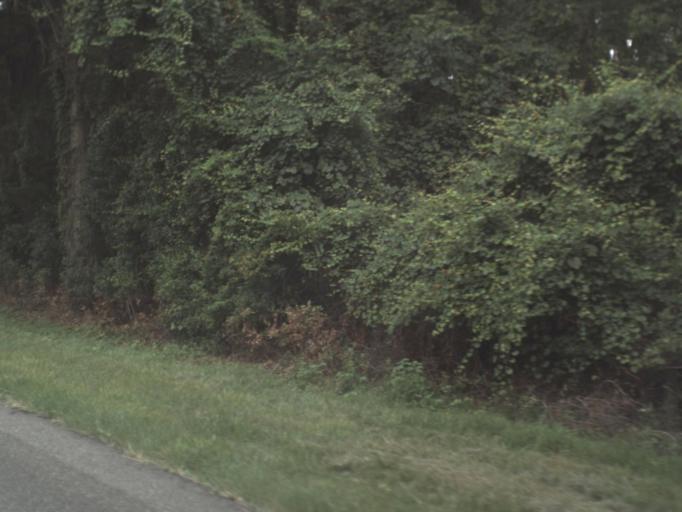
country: US
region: Florida
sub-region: Alachua County
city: Newberry
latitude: 29.5966
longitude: -82.5694
